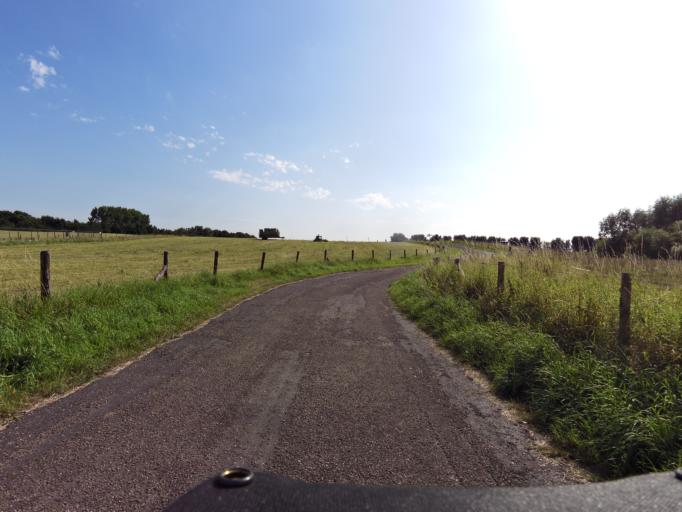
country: NL
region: South Holland
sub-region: Gemeente Binnenmaas
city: Heinenoord
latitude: 51.8296
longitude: 4.4671
